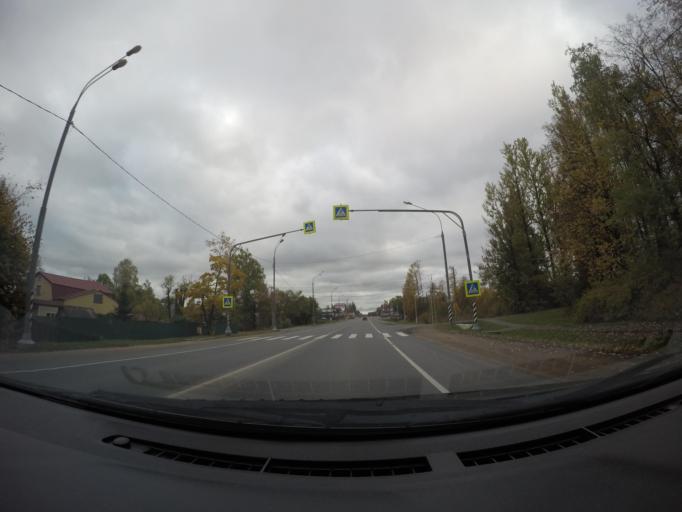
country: RU
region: Moskovskaya
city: Dorokhovo
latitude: 55.6241
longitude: 36.3416
